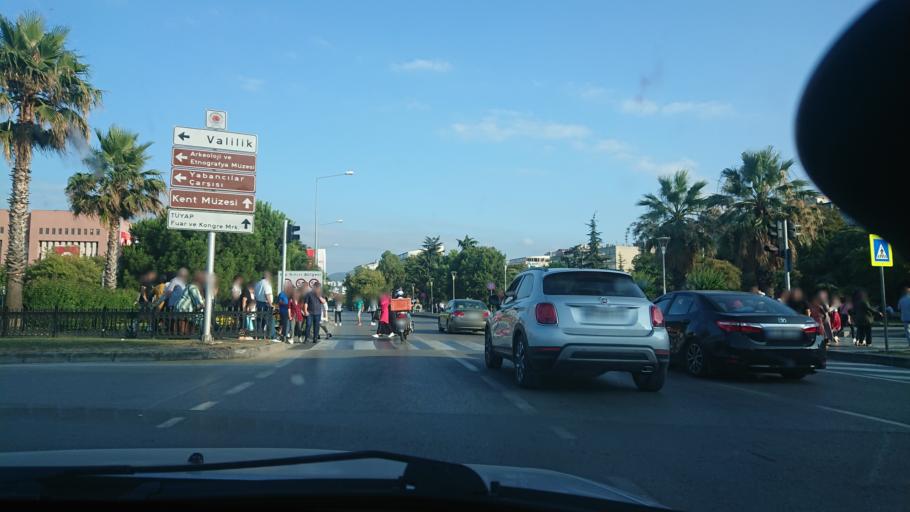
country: TR
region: Samsun
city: Samsun
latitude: 41.2907
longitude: 36.3359
